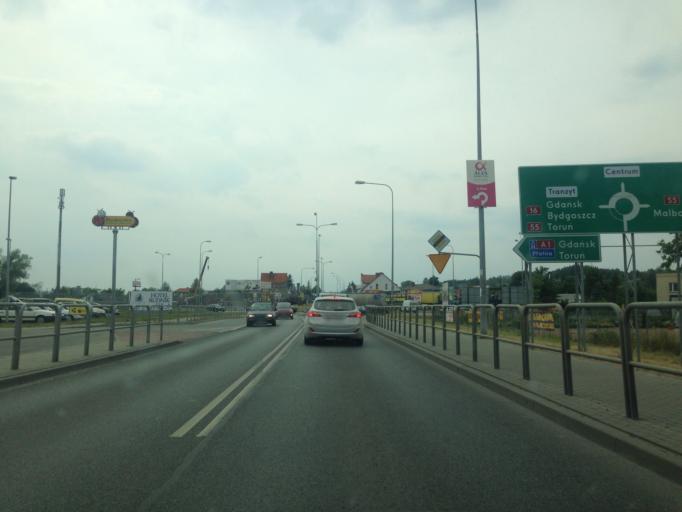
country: PL
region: Kujawsko-Pomorskie
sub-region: Grudziadz
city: Grudziadz
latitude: 53.5038
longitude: 18.8006
